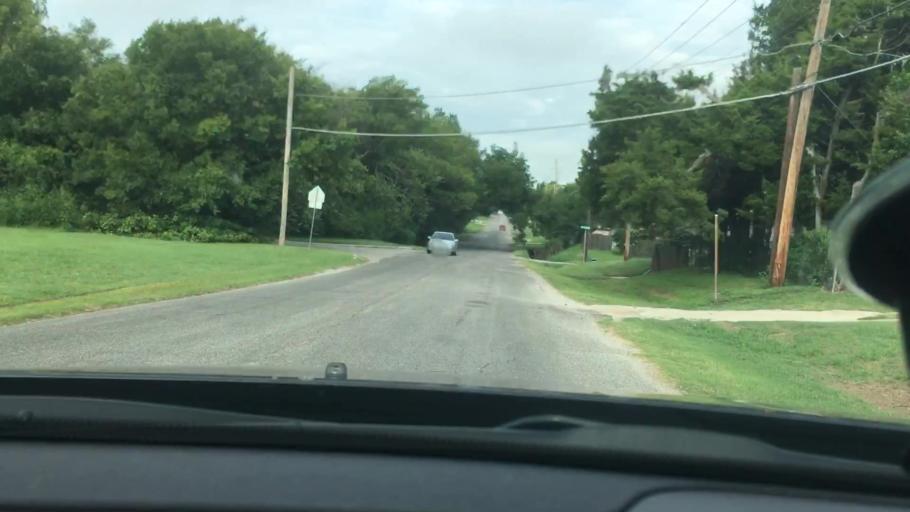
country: US
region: Oklahoma
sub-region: Carter County
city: Ardmore
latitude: 34.1873
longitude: -97.1258
